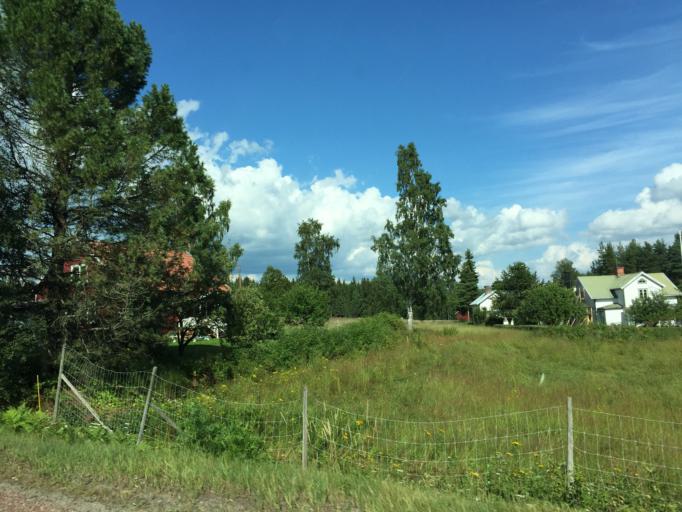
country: SE
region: Gaevleborg
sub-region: Bollnas Kommun
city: Kilafors
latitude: 61.2624
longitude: 16.5517
